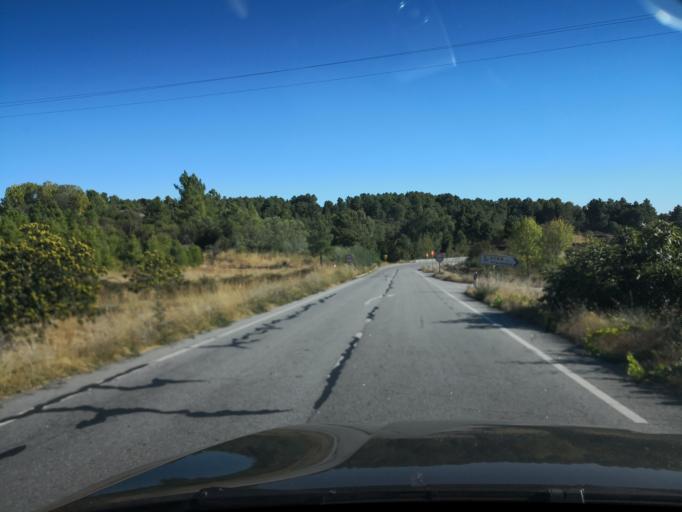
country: PT
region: Vila Real
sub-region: Valpacos
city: Valpacos
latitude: 41.6413
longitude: -7.3169
